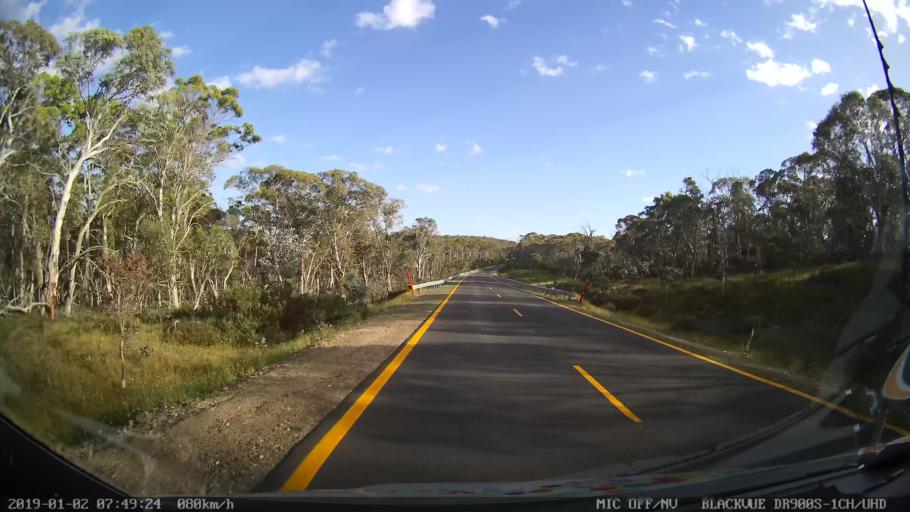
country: AU
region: New South Wales
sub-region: Tumut Shire
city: Tumut
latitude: -35.7421
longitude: 148.5223
